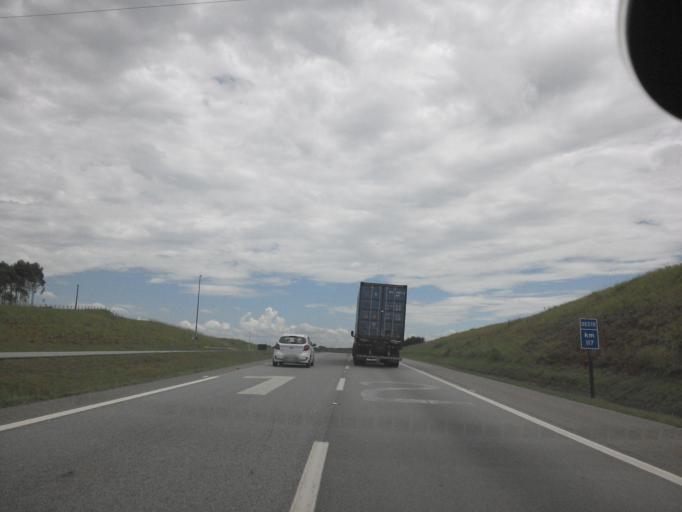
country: BR
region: Sao Paulo
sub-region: Cacapava
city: Cacapava
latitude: -23.1462
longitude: -45.6804
